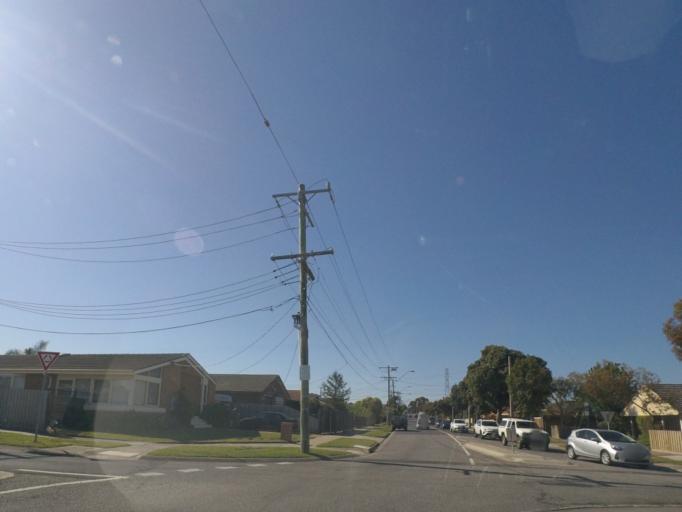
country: AU
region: Victoria
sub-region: Monash
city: Oakleigh South
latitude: -37.9407
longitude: 145.0979
